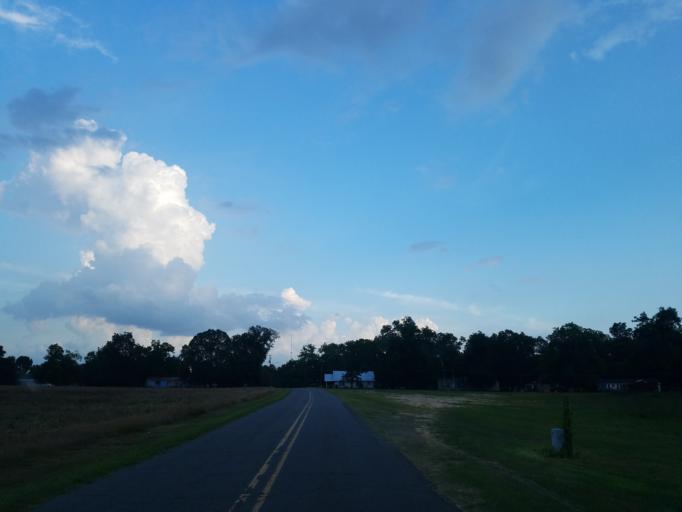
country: US
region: Georgia
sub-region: Dooly County
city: Unadilla
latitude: 32.1930
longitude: -83.7585
